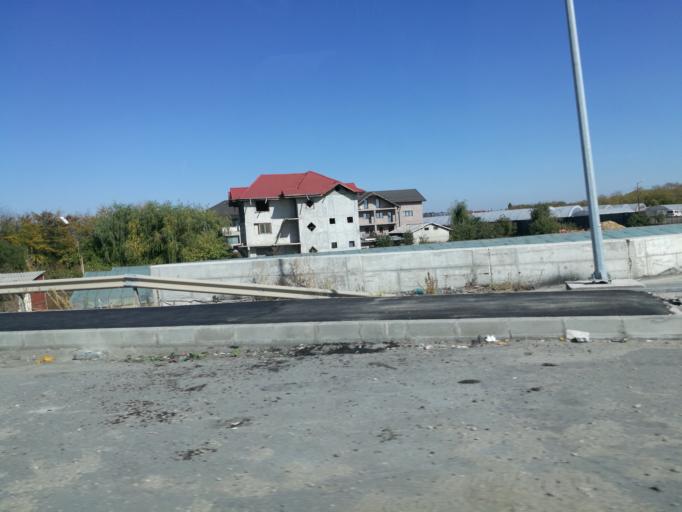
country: RO
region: Ilfov
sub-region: Comuna Chiajna
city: Chiajna
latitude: 44.4541
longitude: 25.9600
